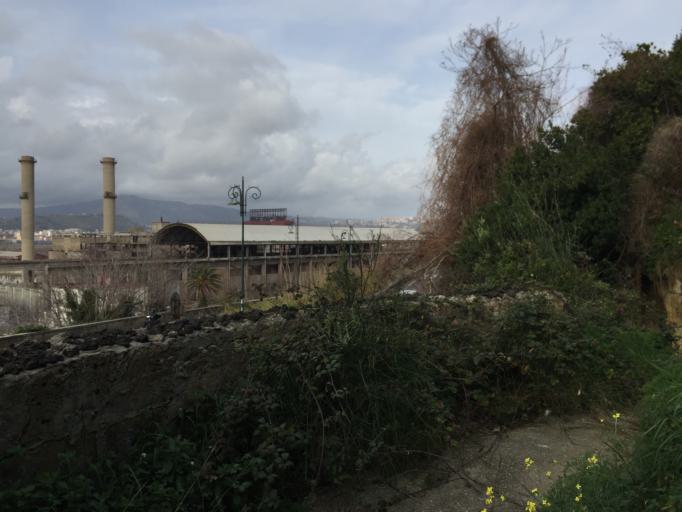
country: IT
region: Campania
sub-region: Provincia di Napoli
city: Bagnoli
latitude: 40.7994
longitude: 14.1755
